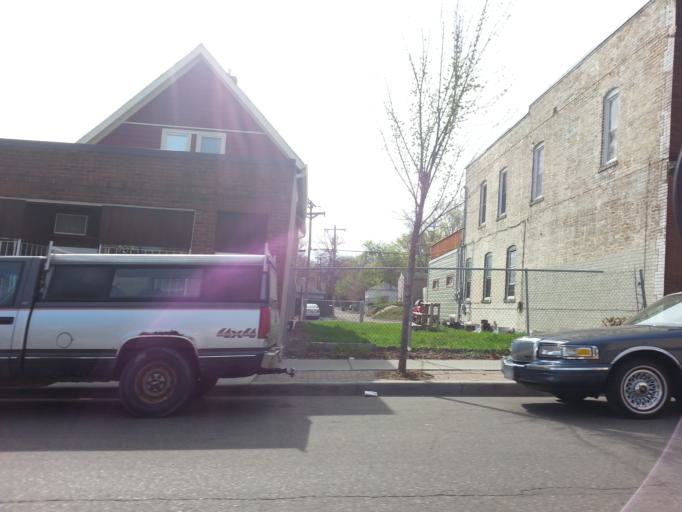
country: US
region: Minnesota
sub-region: Ramsey County
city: Saint Paul
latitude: 44.9742
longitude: -93.0735
